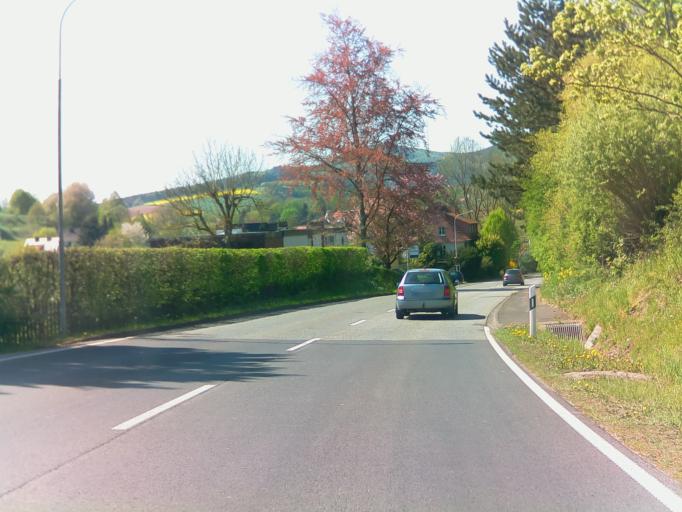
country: DE
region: Hesse
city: Grebenau
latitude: 50.7721
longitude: 9.5264
